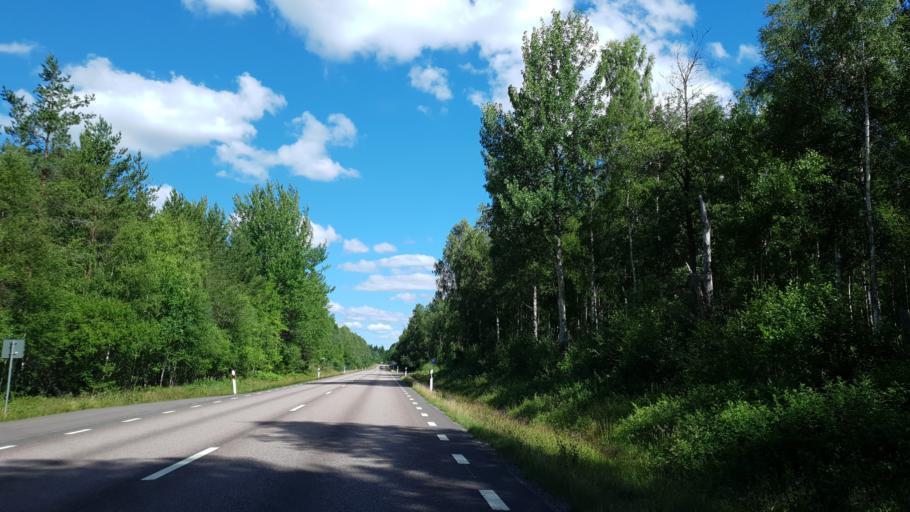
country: SE
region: Kronoberg
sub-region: Lessebo Kommun
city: Lessebo
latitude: 56.8385
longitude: 15.3918
